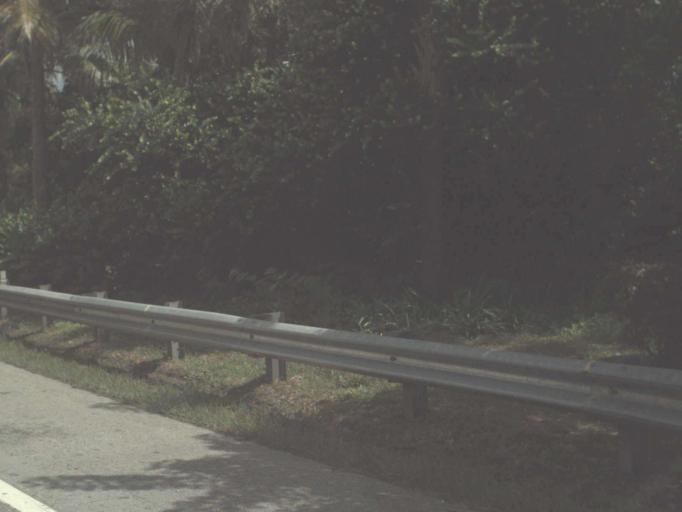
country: US
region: Florida
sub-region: Miami-Dade County
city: Golden Glades
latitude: 25.9239
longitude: -80.2127
